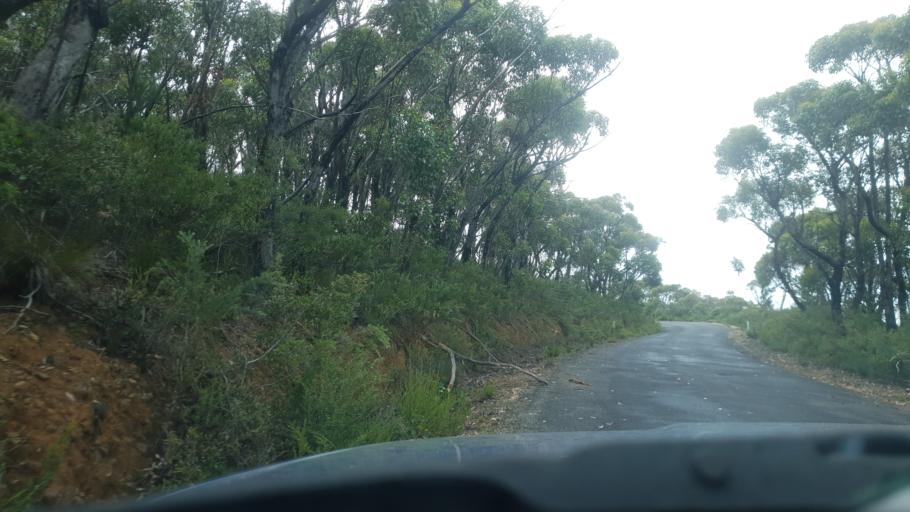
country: AU
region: Victoria
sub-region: Northern Grampians
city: Stawell
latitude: -37.2620
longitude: 142.5738
